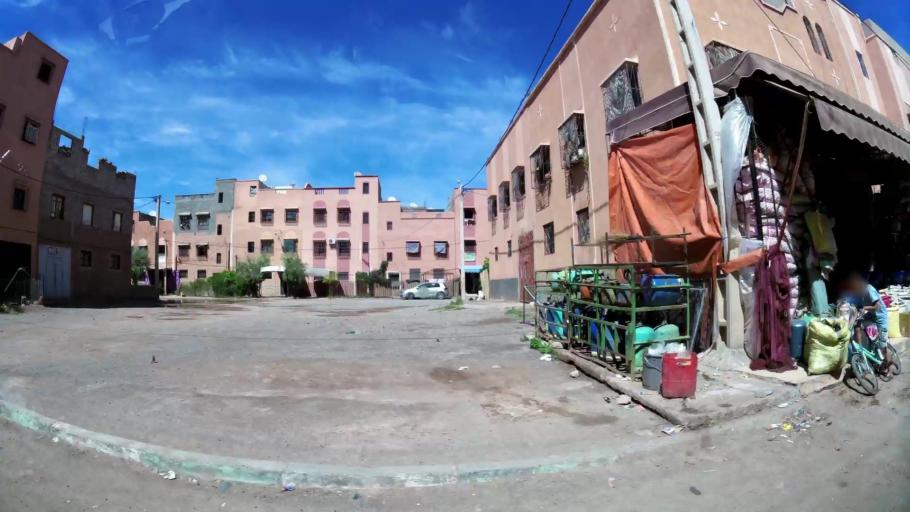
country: MA
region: Marrakech-Tensift-Al Haouz
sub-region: Marrakech
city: Marrakesh
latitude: 31.6433
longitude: -8.1119
